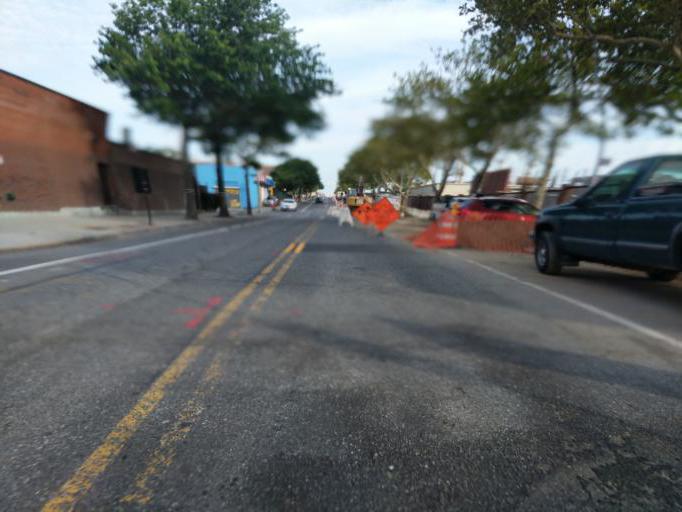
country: US
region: New York
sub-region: Queens County
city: Long Island City
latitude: 40.7801
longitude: -73.9068
